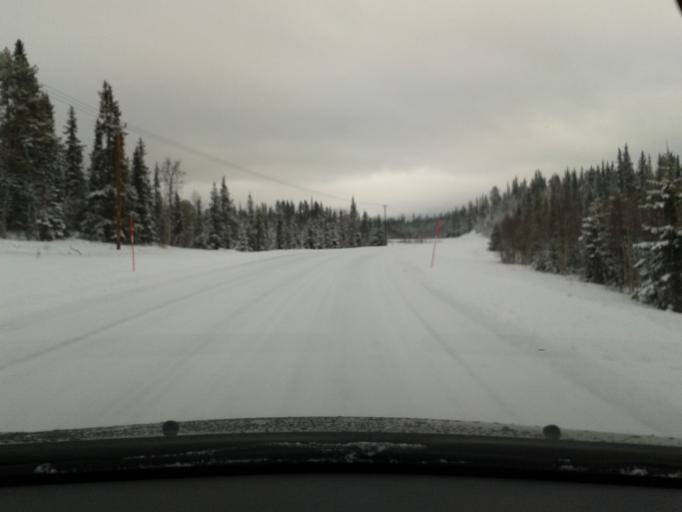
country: SE
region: Vaesterbotten
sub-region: Vilhelmina Kommun
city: Sjoberg
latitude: 65.2421
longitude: 15.7690
